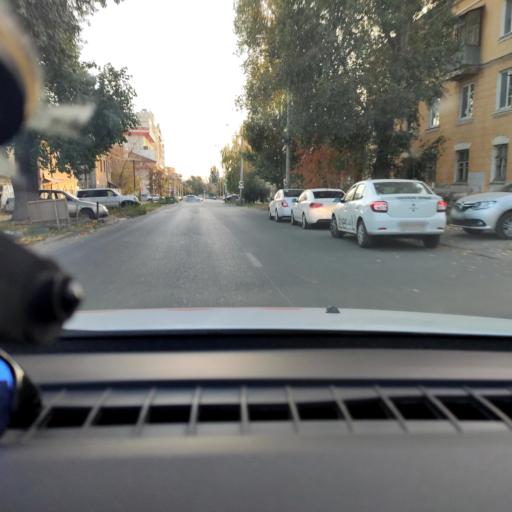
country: RU
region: Samara
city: Samara
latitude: 53.1895
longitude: 50.1108
